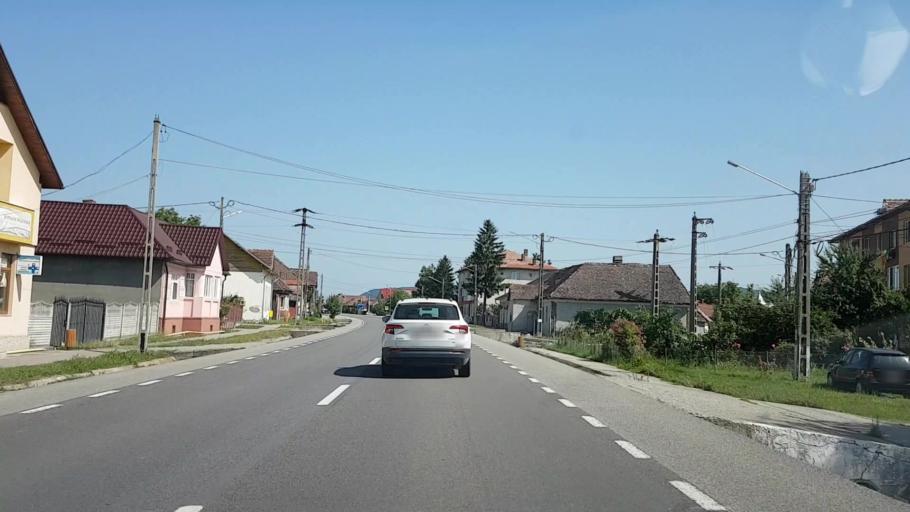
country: RO
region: Bistrita-Nasaud
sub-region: Comuna Sieu-Magherus
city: Sieu-Magherus
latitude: 47.0918
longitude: 24.3720
